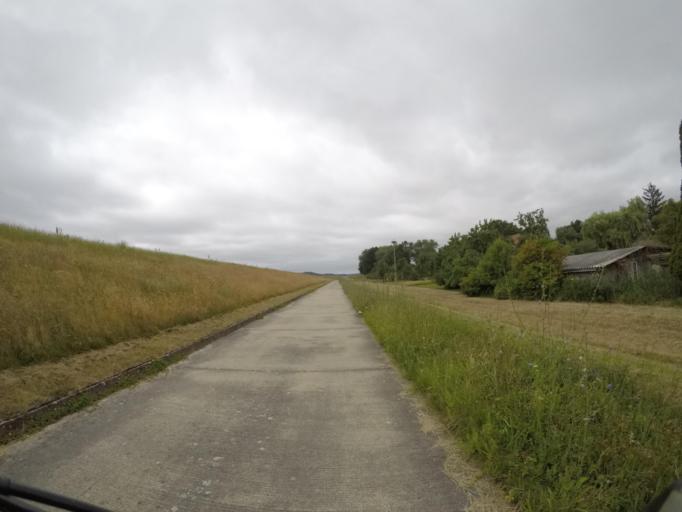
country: DE
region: Lower Saxony
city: Hitzacker
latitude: 53.1529
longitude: 11.0764
